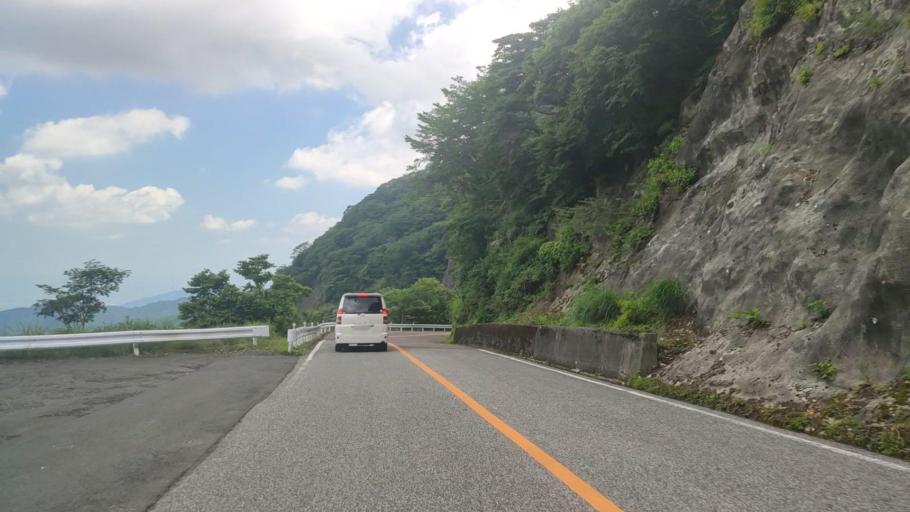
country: JP
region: Gifu
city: Tarui
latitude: 35.4189
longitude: 136.4177
